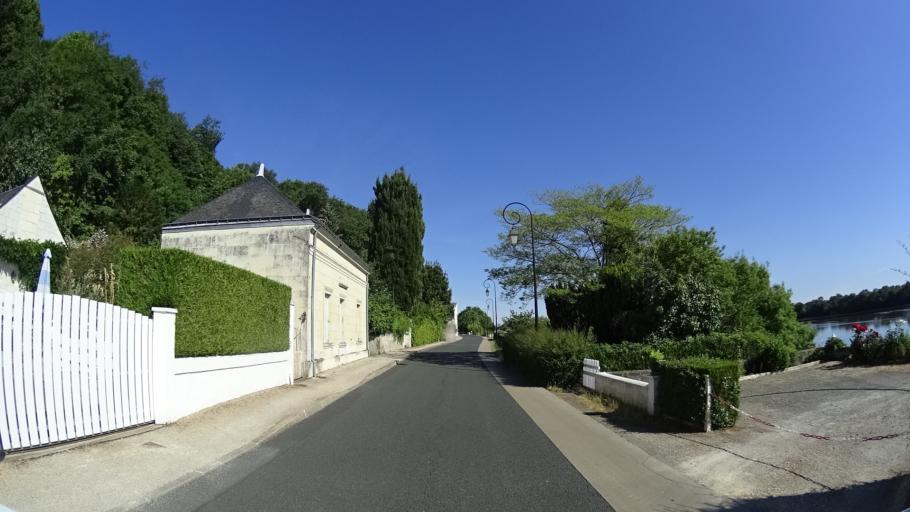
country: FR
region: Pays de la Loire
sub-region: Departement de Maine-et-Loire
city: Saint-Martin-de-la-Place
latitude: 47.2990
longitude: -0.1414
